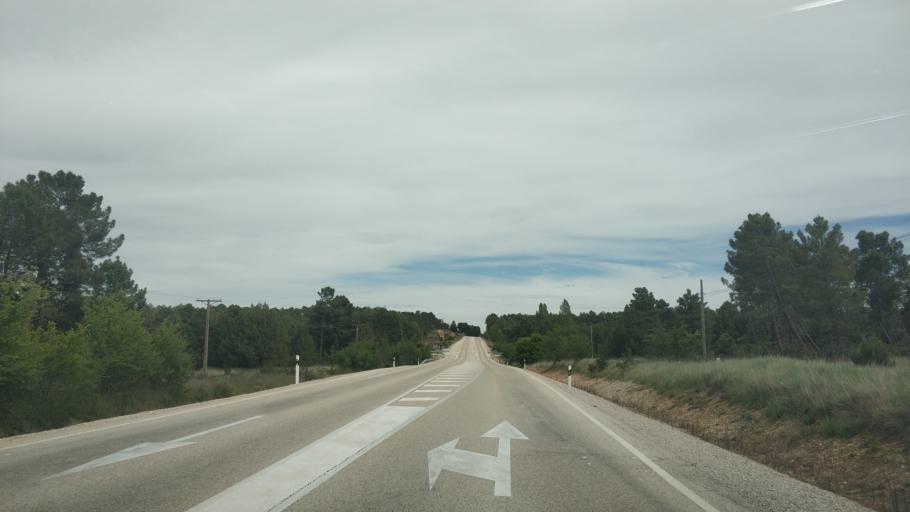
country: ES
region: Castille and Leon
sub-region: Provincia de Soria
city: Valdenebro
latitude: 41.5611
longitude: -2.9761
